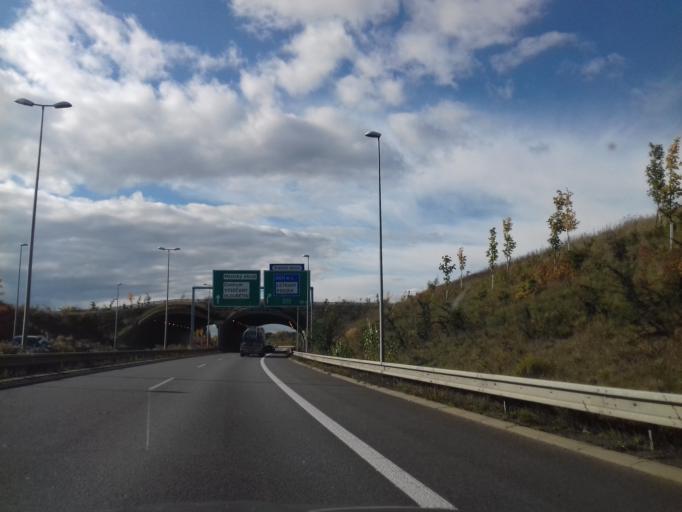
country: CZ
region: Praha
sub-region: Praha 19
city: Kbely
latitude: 50.1156
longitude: 14.5414
